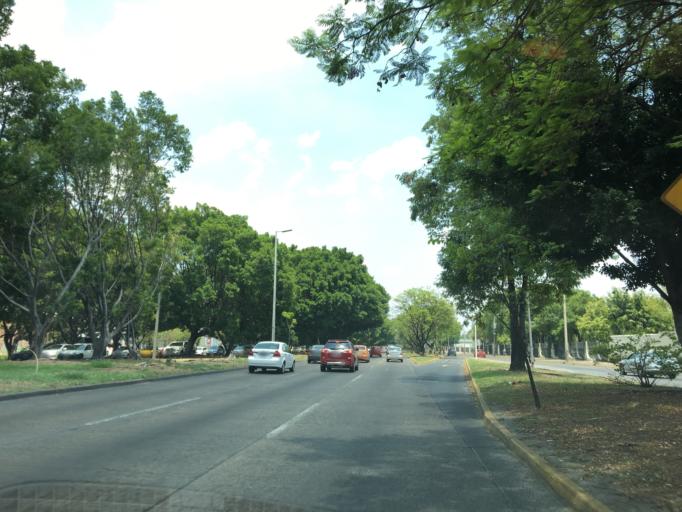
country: MX
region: Jalisco
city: Guadalajara
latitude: 20.6460
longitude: -103.3593
